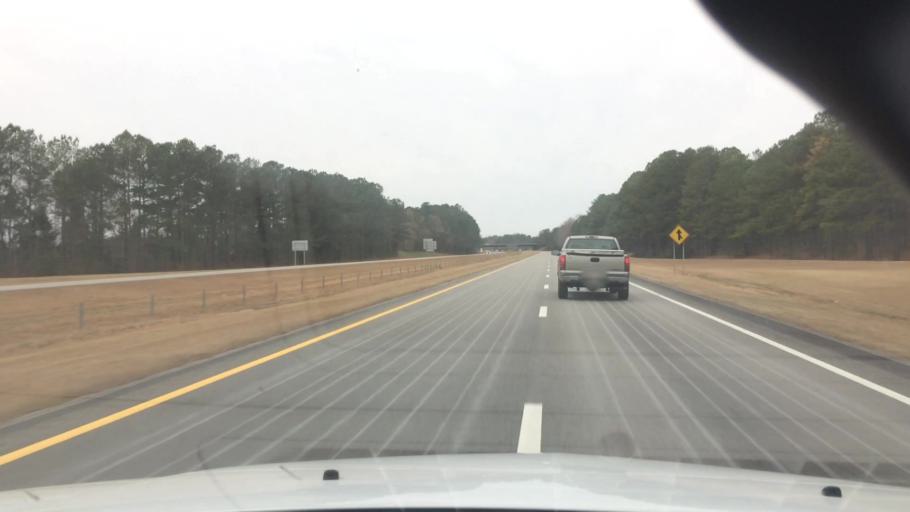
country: US
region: North Carolina
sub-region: Nash County
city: Spring Hope
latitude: 35.9320
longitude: -78.0999
